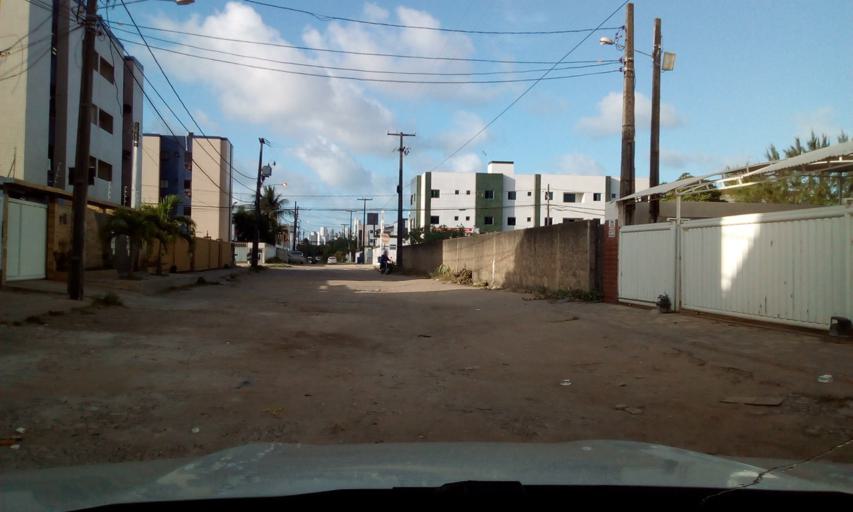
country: BR
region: Paraiba
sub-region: Joao Pessoa
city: Joao Pessoa
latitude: -7.1564
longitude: -34.8280
